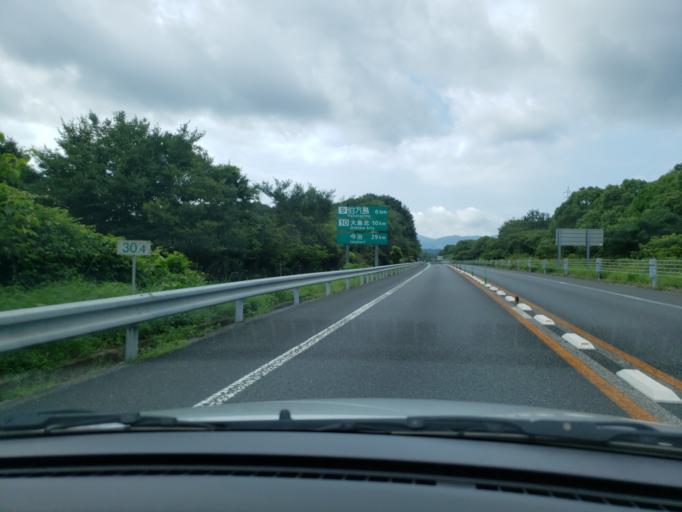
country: JP
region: Hiroshima
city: Innoshima
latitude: 34.2424
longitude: 133.0478
